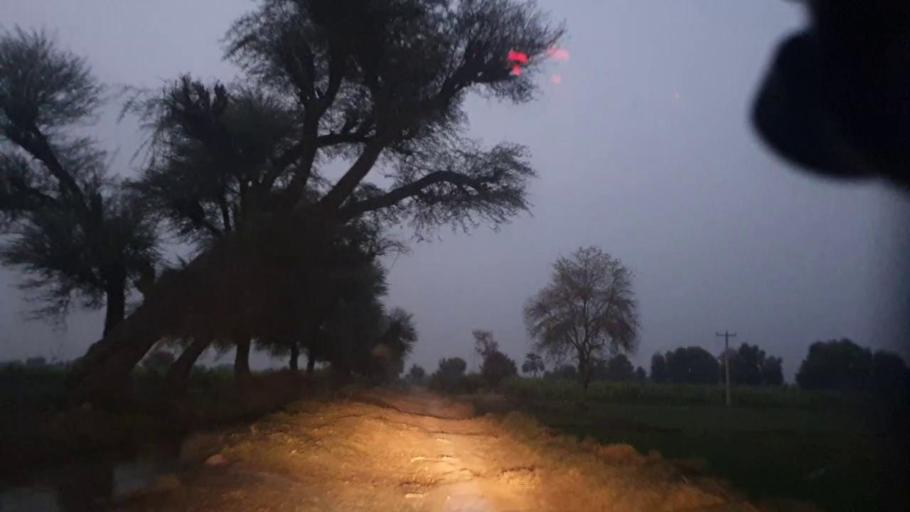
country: PK
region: Sindh
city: Hingorja
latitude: 27.2047
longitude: 68.3715
